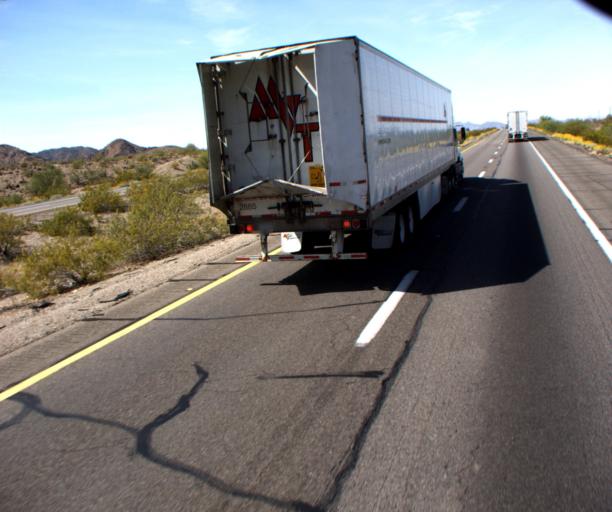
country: US
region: Arizona
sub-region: La Paz County
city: Quartzsite
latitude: 33.6789
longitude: -114.0716
